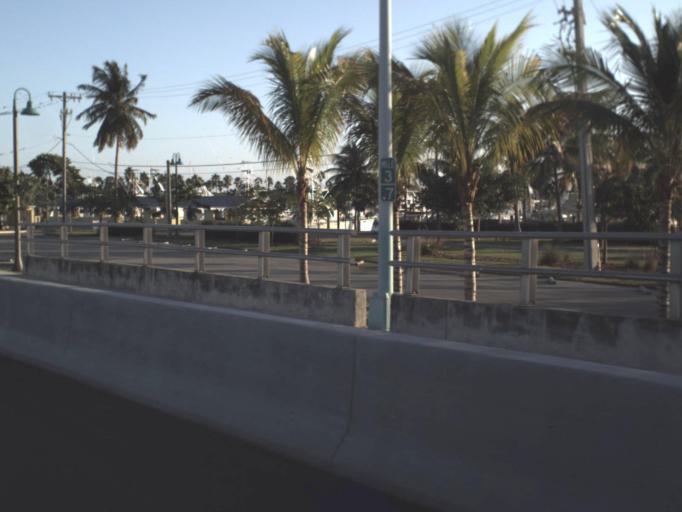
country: US
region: Florida
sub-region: Miami-Dade County
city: Key Biscayne
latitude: 25.7278
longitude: -80.1559
